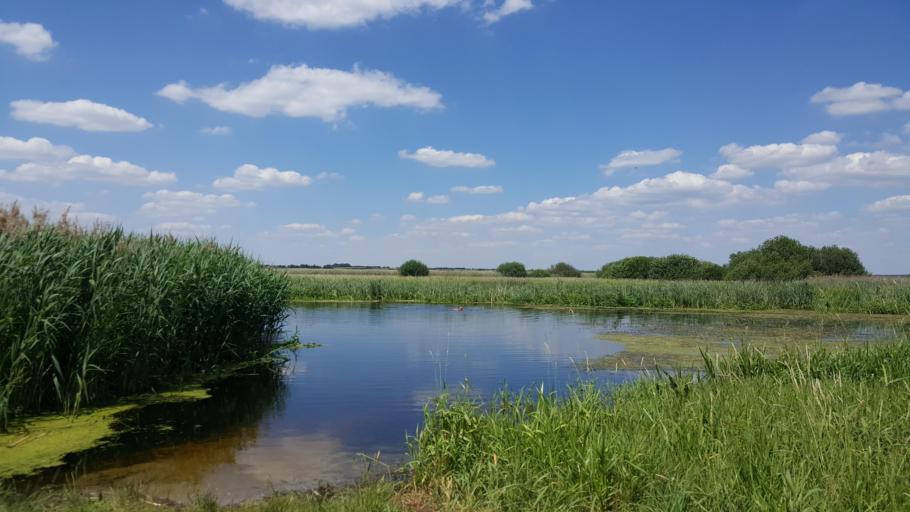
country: BY
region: Brest
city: Kamyanyets
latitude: 52.4061
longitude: 23.8188
